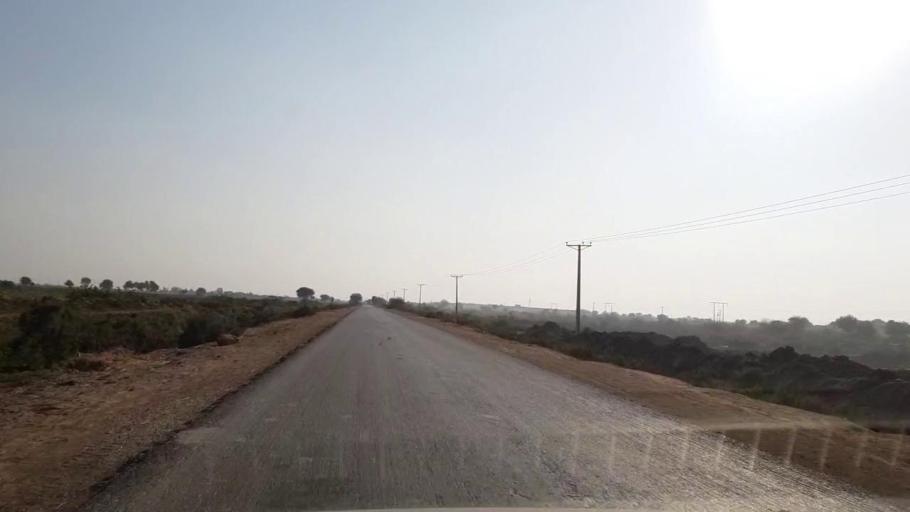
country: PK
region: Sindh
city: Bulri
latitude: 24.9117
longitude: 68.3483
